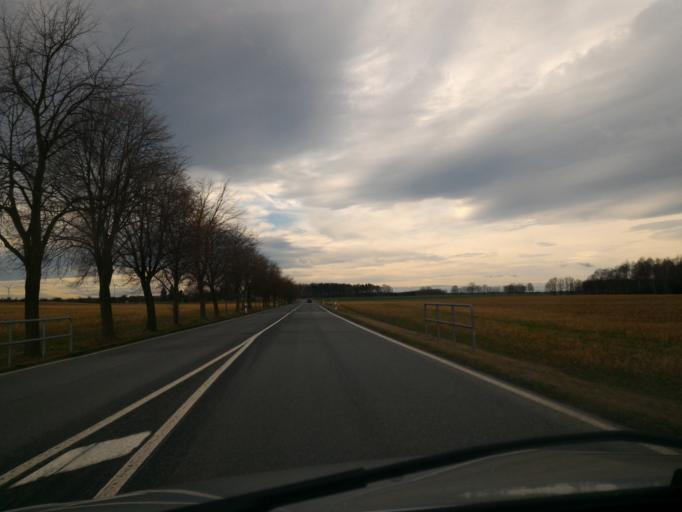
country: DE
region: Saxony
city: Grossharthau
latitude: 51.0927
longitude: 14.0687
